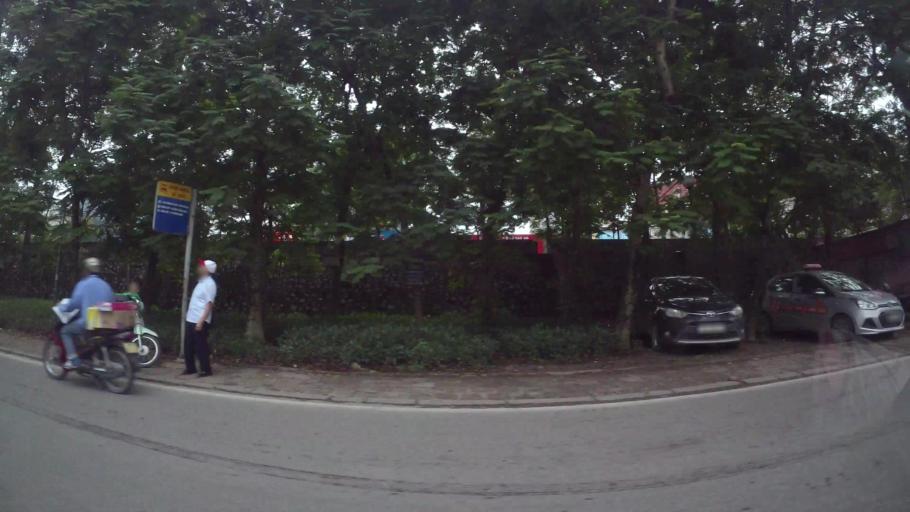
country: VN
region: Ha Noi
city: Hai BaTrung
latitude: 21.0149
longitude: 105.8626
